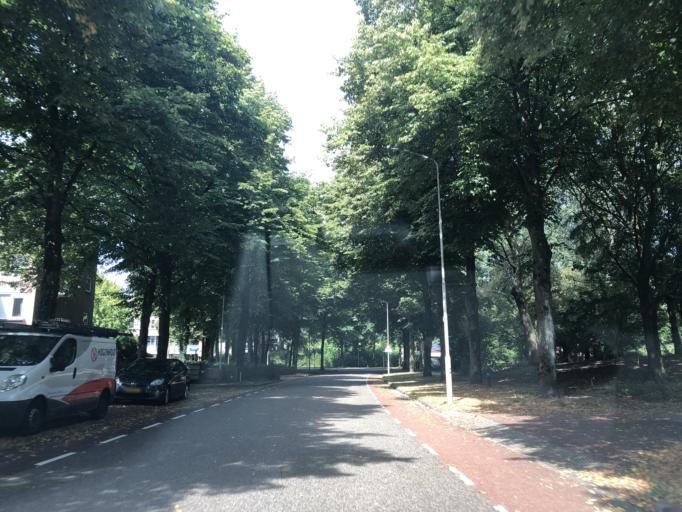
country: NL
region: Gelderland
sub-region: Gemeente Wageningen
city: Wageningen
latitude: 51.9797
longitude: 5.6736
